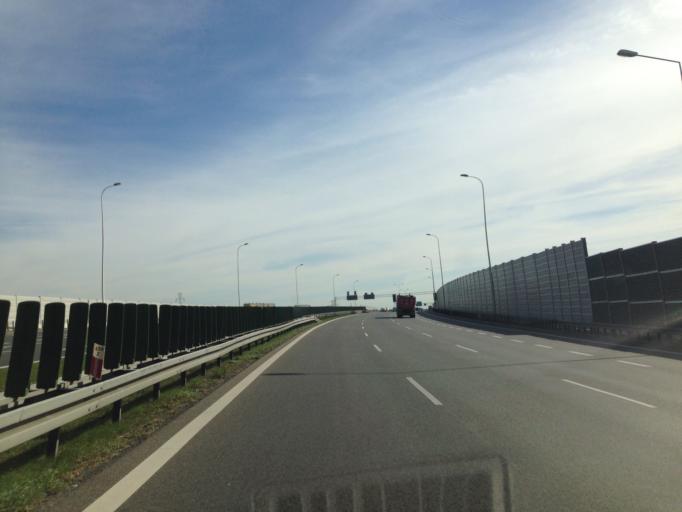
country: PL
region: Masovian Voivodeship
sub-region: Powiat pruszkowski
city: Piastow
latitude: 52.1981
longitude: 20.8501
